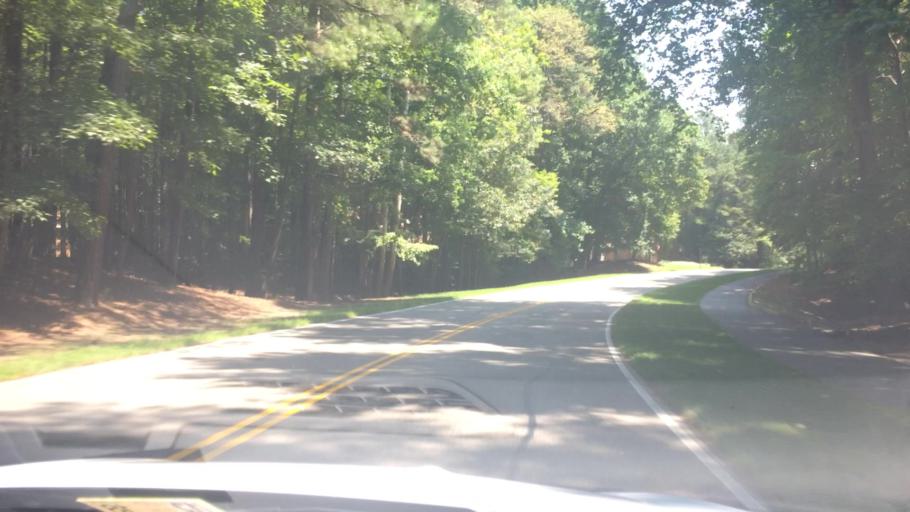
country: US
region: Virginia
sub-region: City of Williamsburg
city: Williamsburg
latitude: 37.2460
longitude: -76.6712
